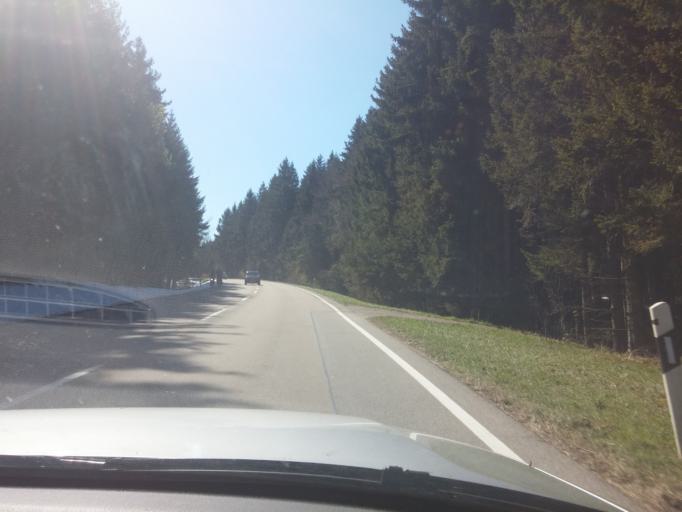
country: DE
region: Baden-Wuerttemberg
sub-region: Tuebingen Region
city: Bad Wurzach
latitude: 47.9218
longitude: 9.9573
